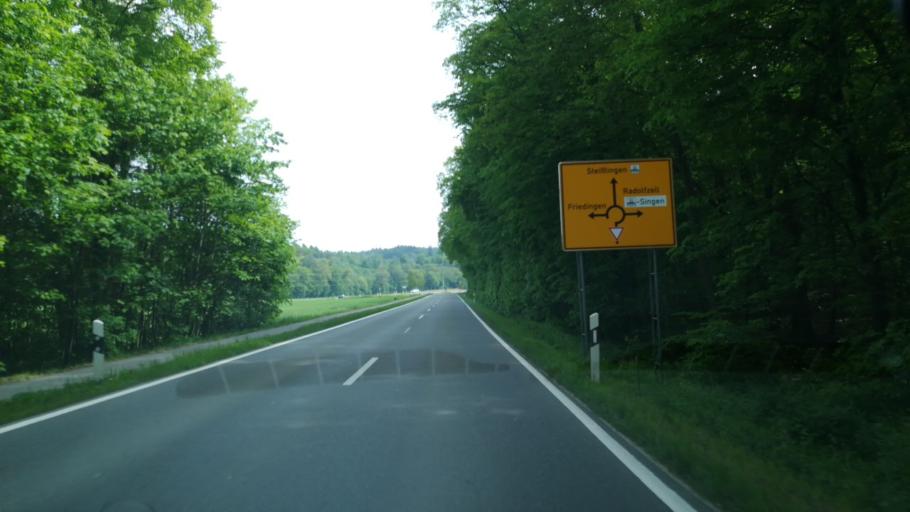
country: DE
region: Baden-Wuerttemberg
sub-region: Freiburg Region
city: Volkertshausen
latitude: 47.7730
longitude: 8.8874
